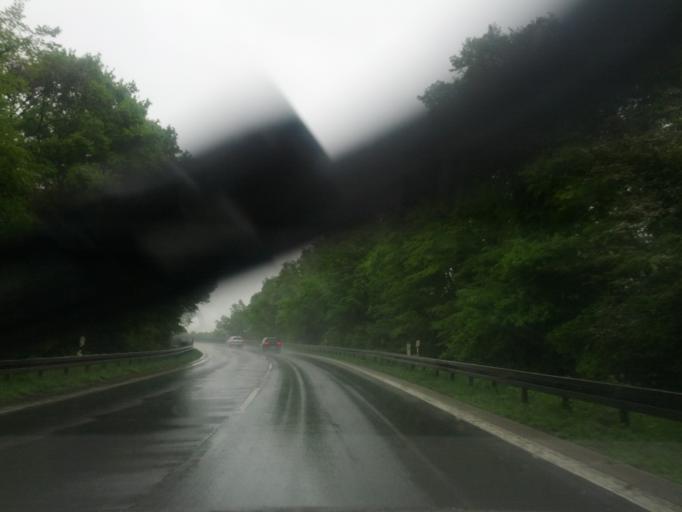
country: DE
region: North Rhine-Westphalia
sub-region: Regierungsbezirk Koln
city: Ostheim
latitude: 50.9216
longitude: 7.0575
